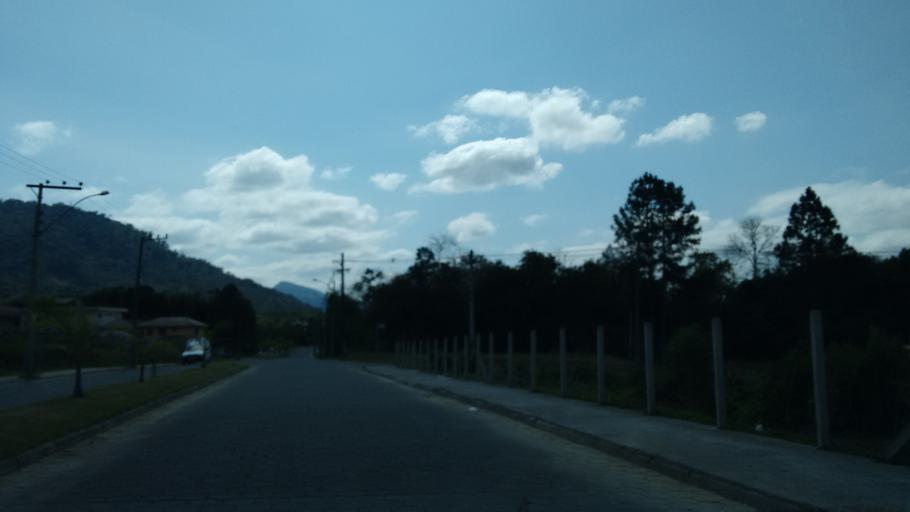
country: BR
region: Santa Catarina
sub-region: Pomerode
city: Pomerode
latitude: -26.7570
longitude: -49.1739
